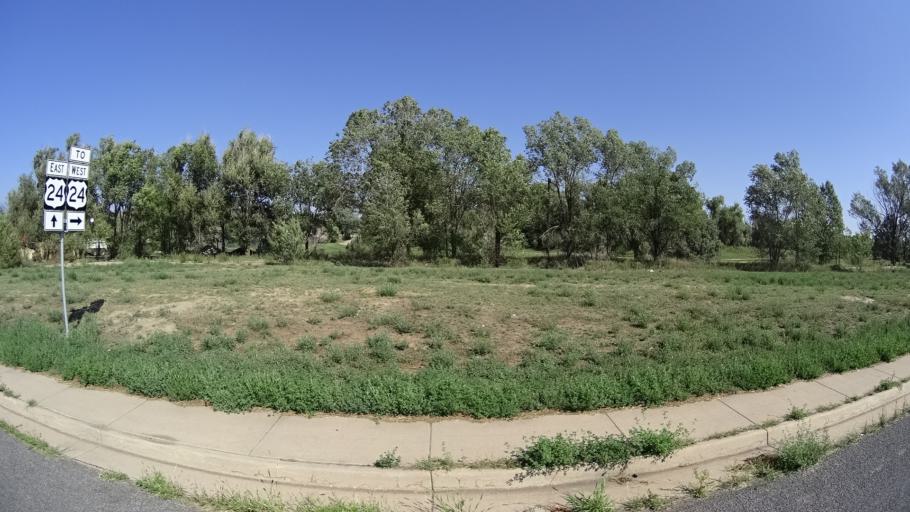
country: US
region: Colorado
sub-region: El Paso County
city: Stratmoor
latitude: 38.8180
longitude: -104.7781
